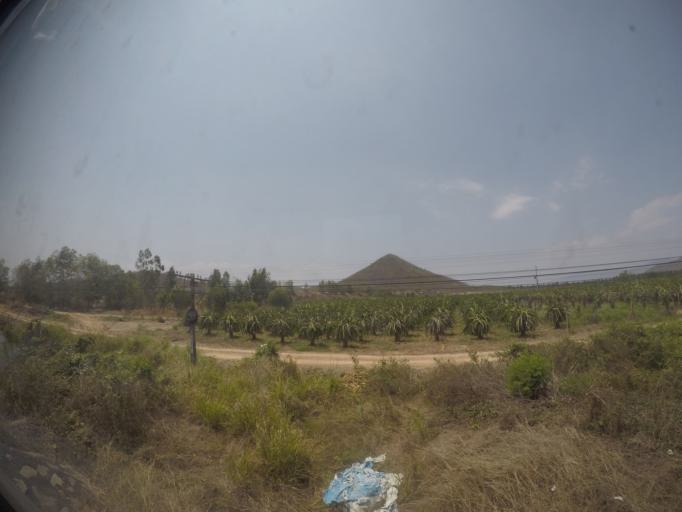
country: VN
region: Binh Thuan
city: Thuan Nam
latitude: 10.9409
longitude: 107.9714
